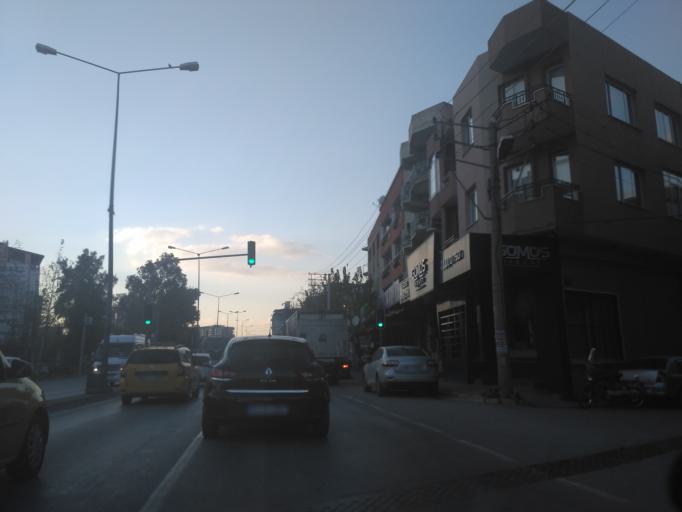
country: TR
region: Izmir
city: Buca
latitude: 38.4293
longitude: 27.2043
